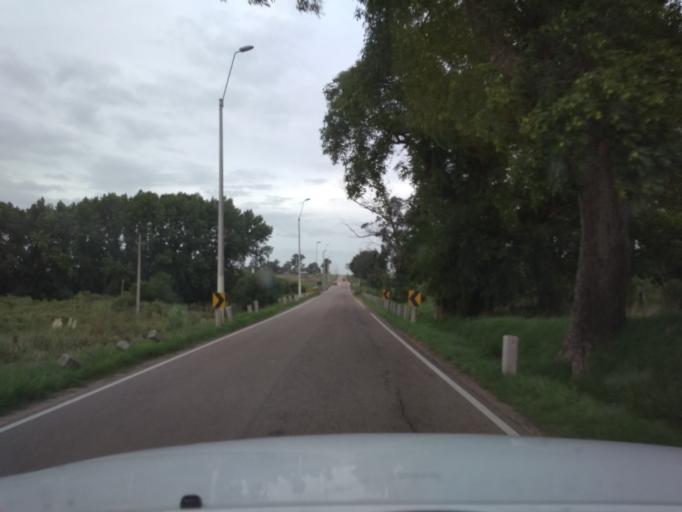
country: UY
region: Canelones
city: Tala
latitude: -34.3544
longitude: -55.7705
